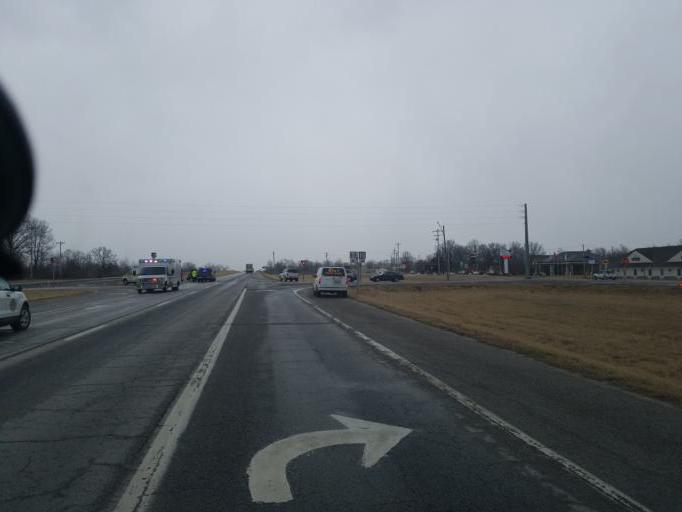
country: US
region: Missouri
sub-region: Macon County
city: La Plata
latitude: 40.0354
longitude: -92.4894
